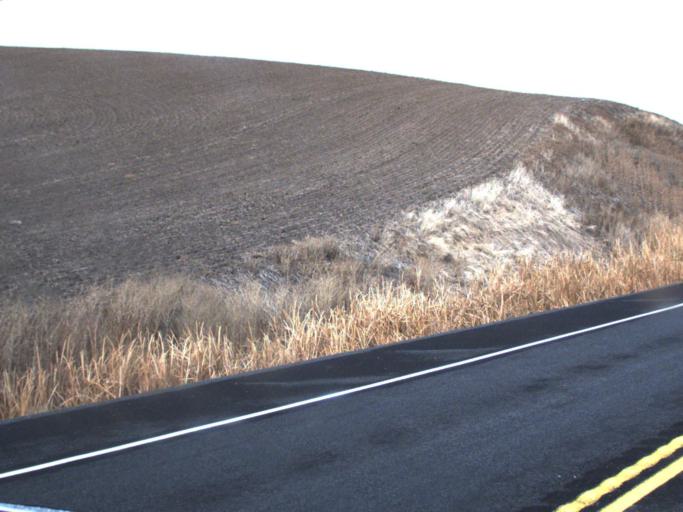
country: US
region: Washington
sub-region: Whitman County
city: Pullman
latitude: 46.6071
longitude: -117.1638
